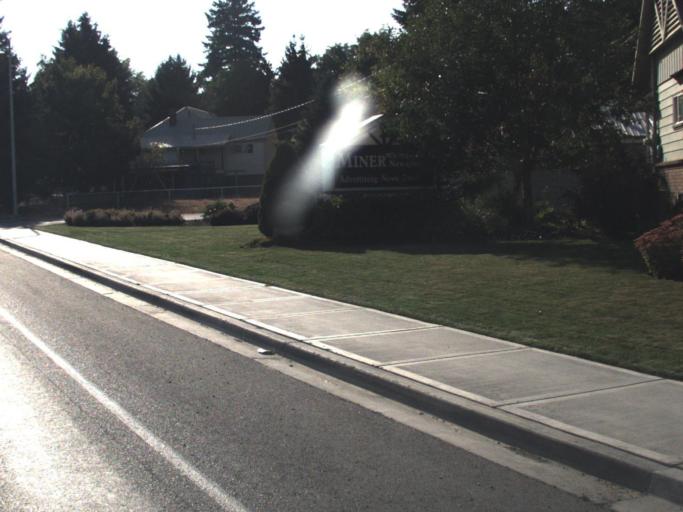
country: US
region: Washington
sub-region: Pend Oreille County
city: Newport
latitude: 48.1773
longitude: -117.0457
